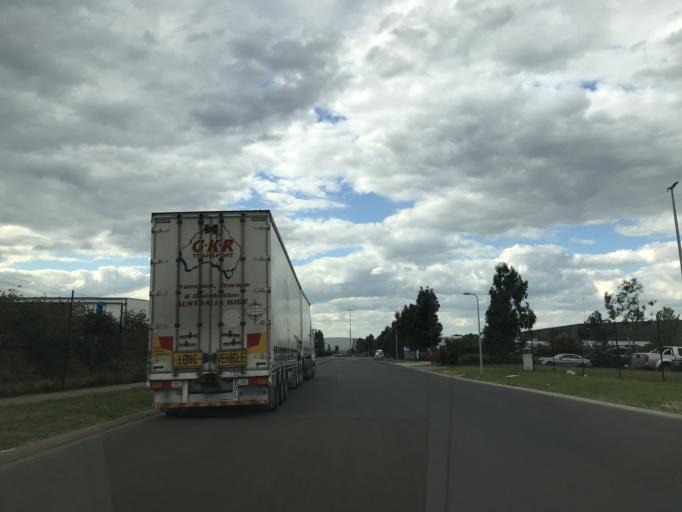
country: AU
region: Victoria
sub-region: Wyndham
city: Truganina
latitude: -37.8227
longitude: 144.7446
